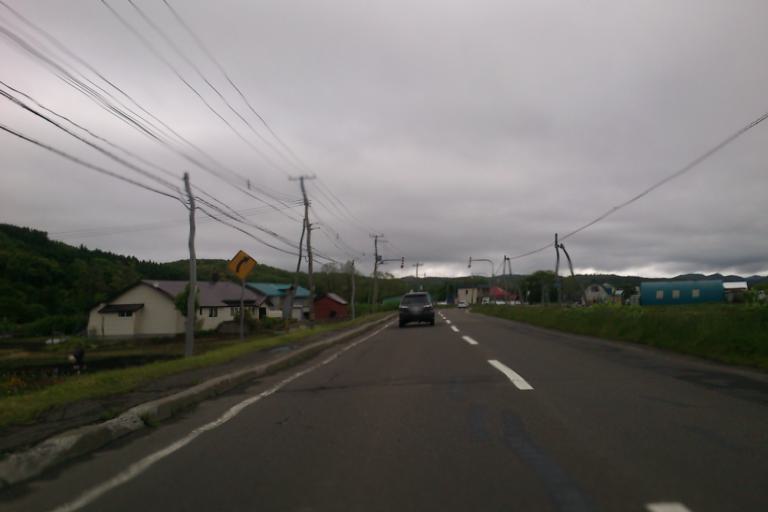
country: JP
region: Hokkaido
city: Ishikari
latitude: 43.3187
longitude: 141.4285
